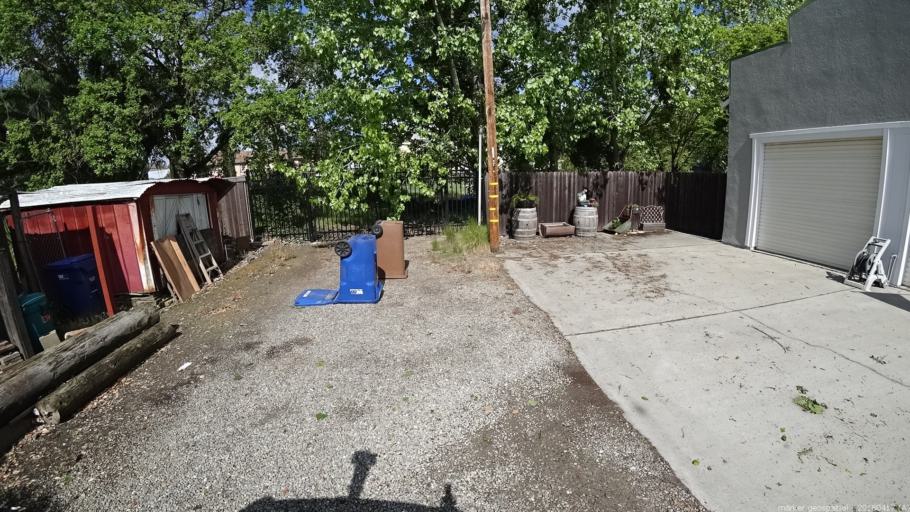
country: US
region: California
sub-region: Sacramento County
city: Walnut Grove
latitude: 38.2437
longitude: -121.5108
